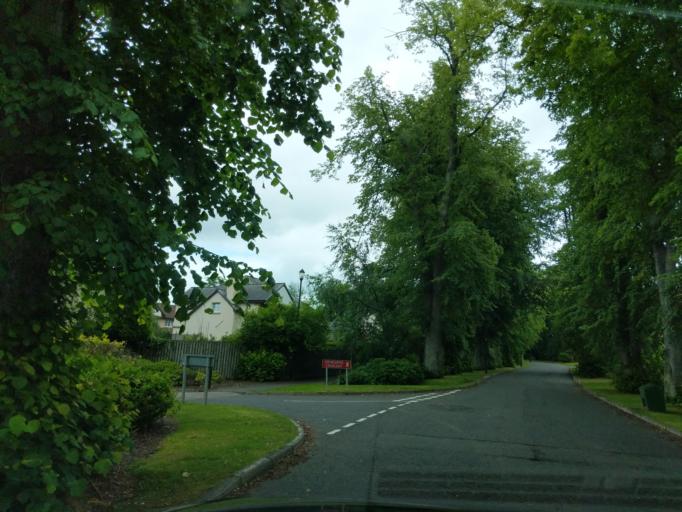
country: GB
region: Scotland
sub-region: The Scottish Borders
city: Peebles
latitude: 55.6437
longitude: -3.1981
